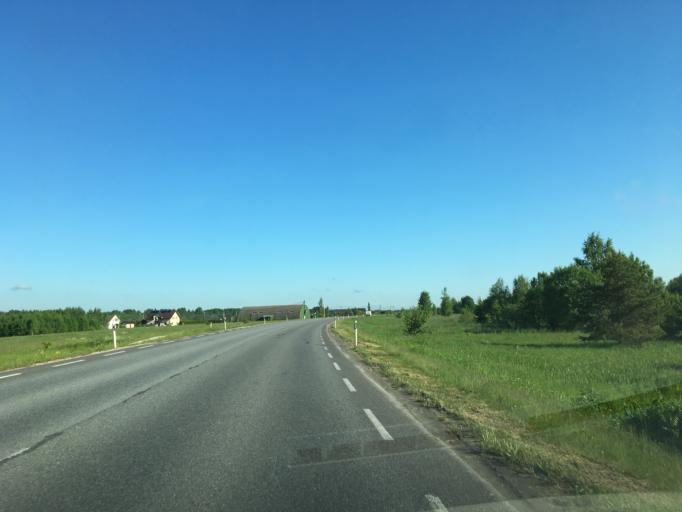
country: EE
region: Tartu
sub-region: Tartu linn
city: Tartu
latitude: 58.4310
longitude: 26.6826
